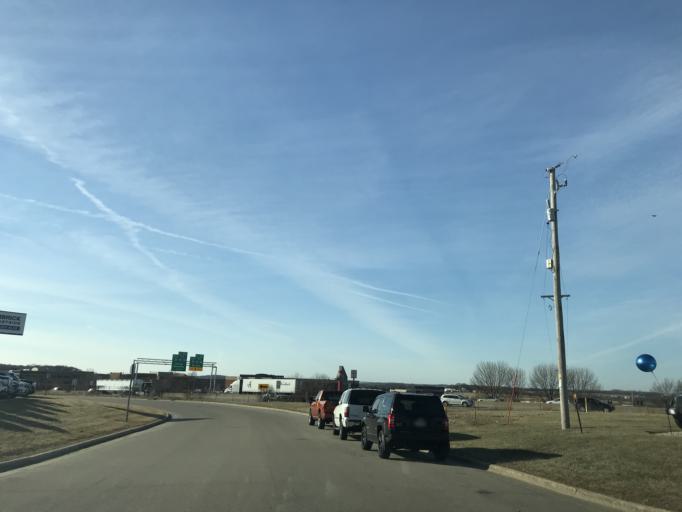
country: US
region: Wisconsin
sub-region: Dane County
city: Sun Prairie
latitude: 43.1431
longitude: -89.2872
